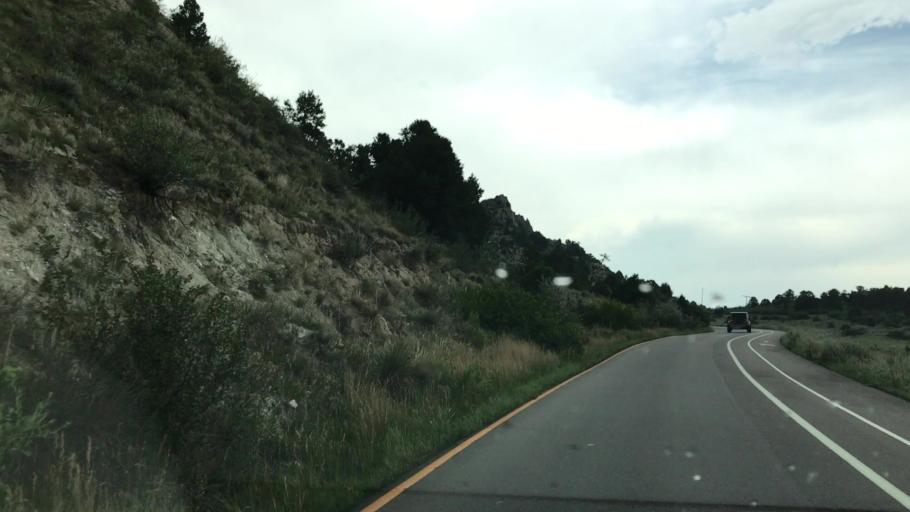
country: US
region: Colorado
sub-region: El Paso County
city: Manitou Springs
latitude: 38.8792
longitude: -104.8782
